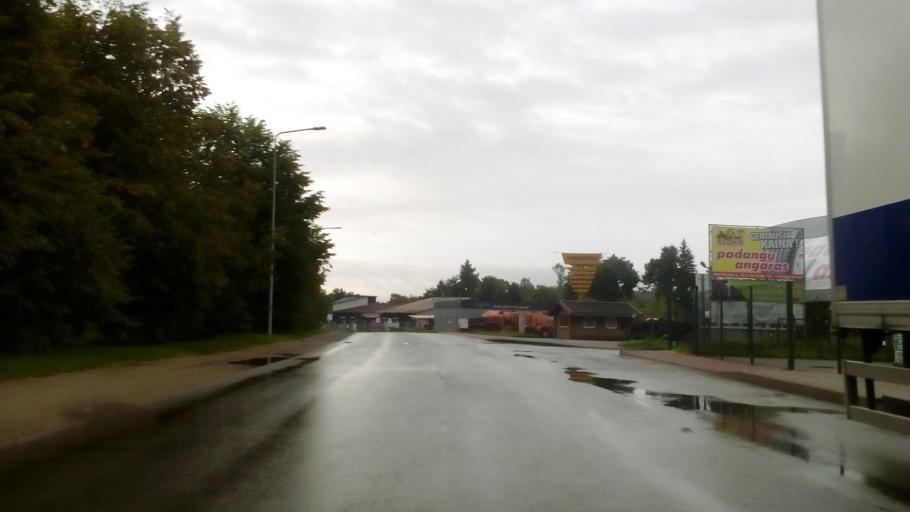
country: LT
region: Alytaus apskritis
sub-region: Alytus
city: Alytus
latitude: 54.3909
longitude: 24.0376
